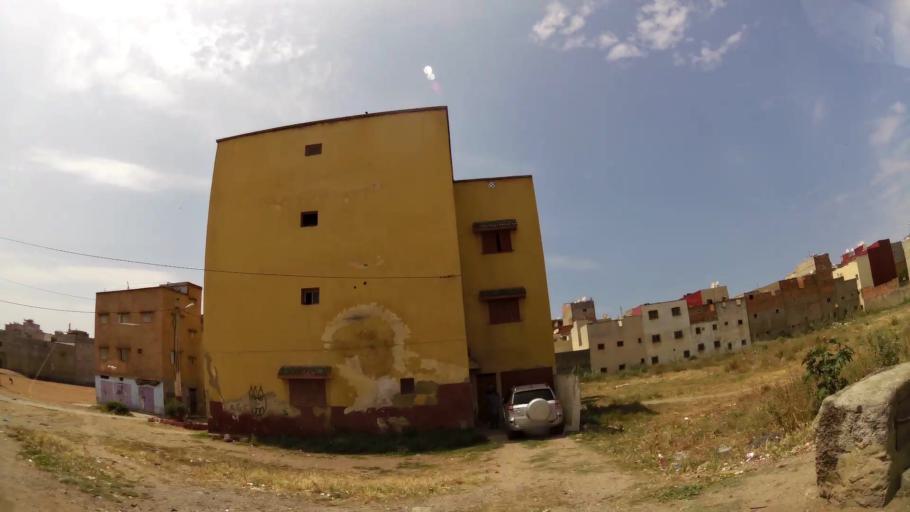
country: MA
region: Rabat-Sale-Zemmour-Zaer
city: Sale
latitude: 34.0559
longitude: -6.8163
